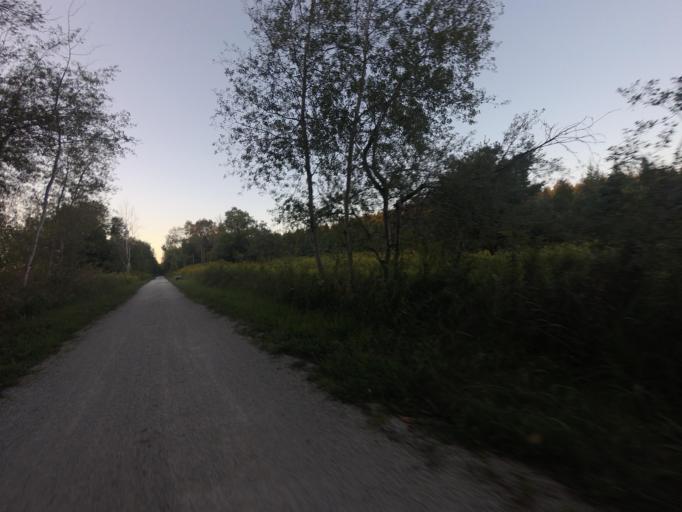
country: CA
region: Ontario
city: Orangeville
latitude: 43.9281
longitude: -79.8434
